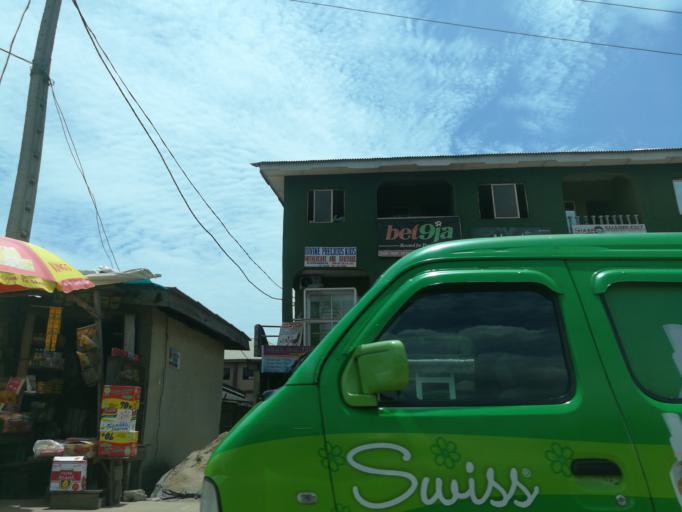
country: NG
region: Lagos
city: Ebute Ikorodu
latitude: 6.6022
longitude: 3.4910
